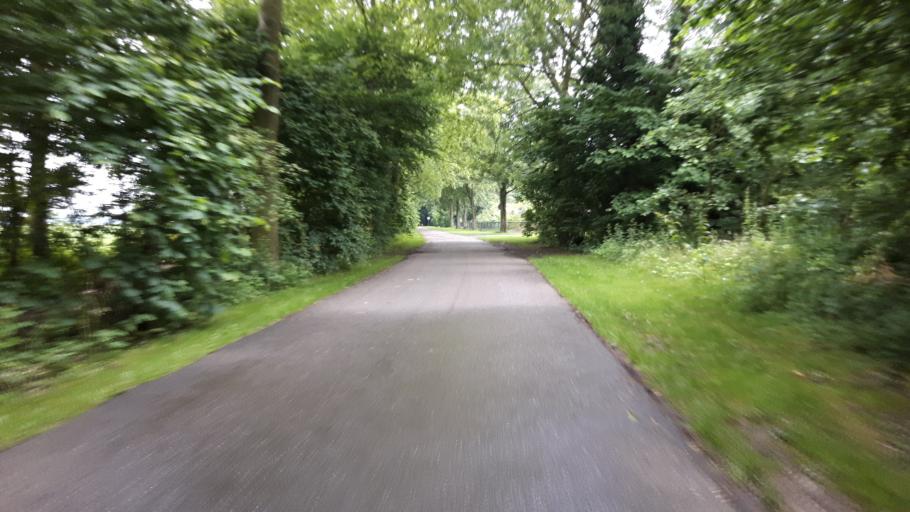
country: NL
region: Utrecht
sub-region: Gemeente Lopik
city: Lopik
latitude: 51.9698
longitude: 4.9595
